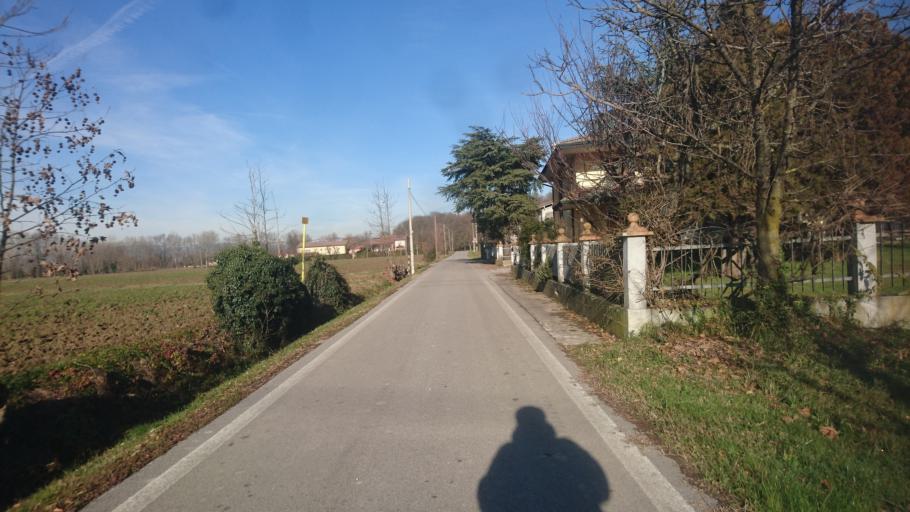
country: IT
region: Veneto
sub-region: Provincia di Padova
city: Piazzola sul Brenta
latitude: 45.5185
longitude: 11.7783
